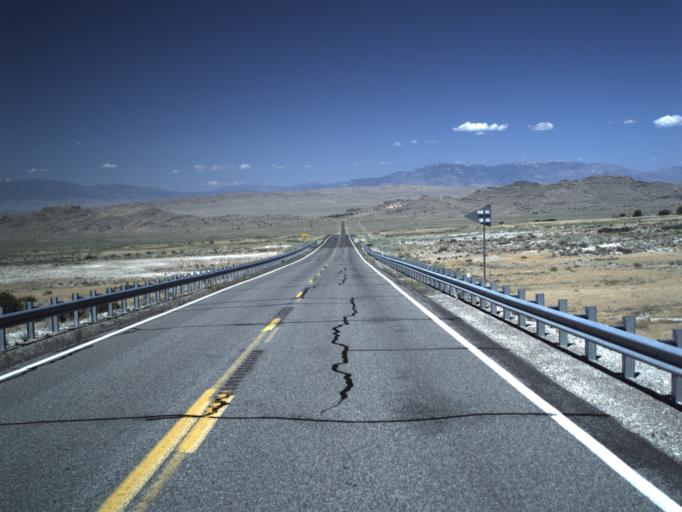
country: US
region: Utah
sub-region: Beaver County
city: Milford
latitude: 39.0716
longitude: -113.6580
